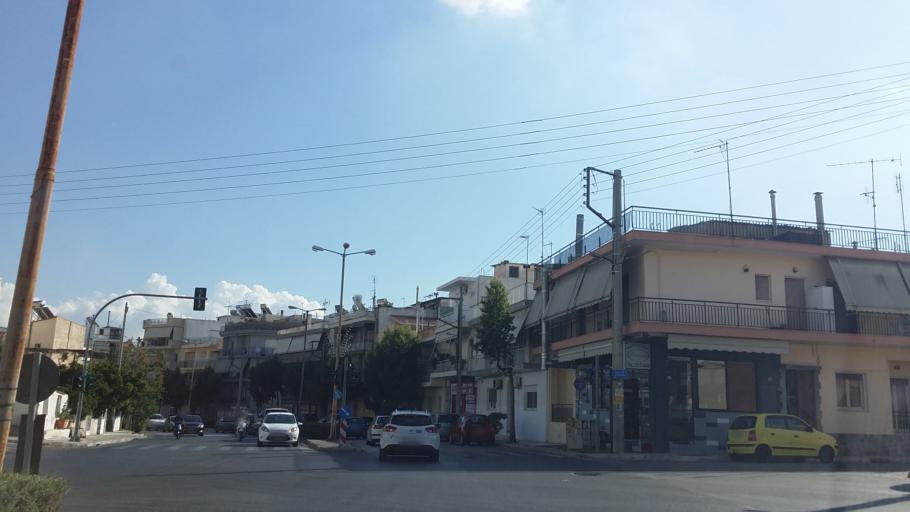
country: GR
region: Attica
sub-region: Nomarchia Athinas
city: Ilion
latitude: 38.0233
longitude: 23.7034
